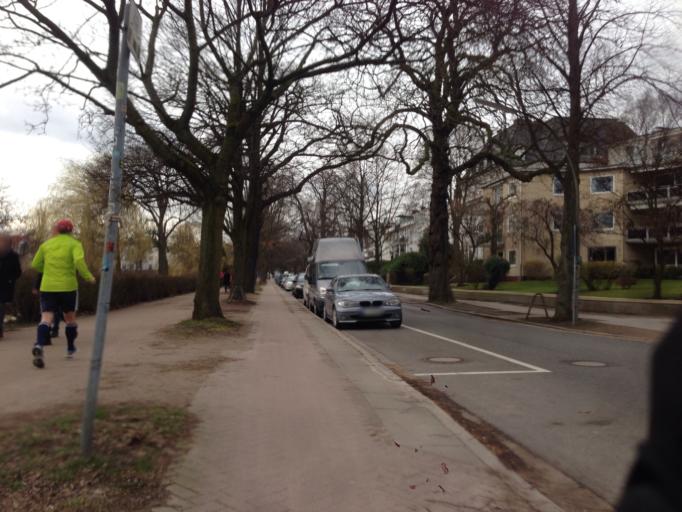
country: DE
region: Hamburg
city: Hamburg
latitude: 53.5780
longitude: 10.0039
